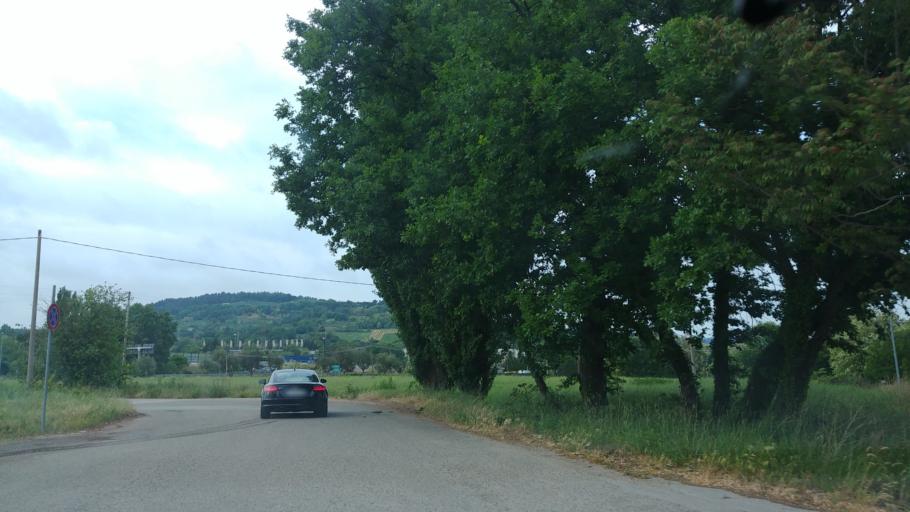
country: IT
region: The Marches
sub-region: Provincia di Pesaro e Urbino
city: Villa Ceccolini
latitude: 43.8964
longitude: 12.8430
